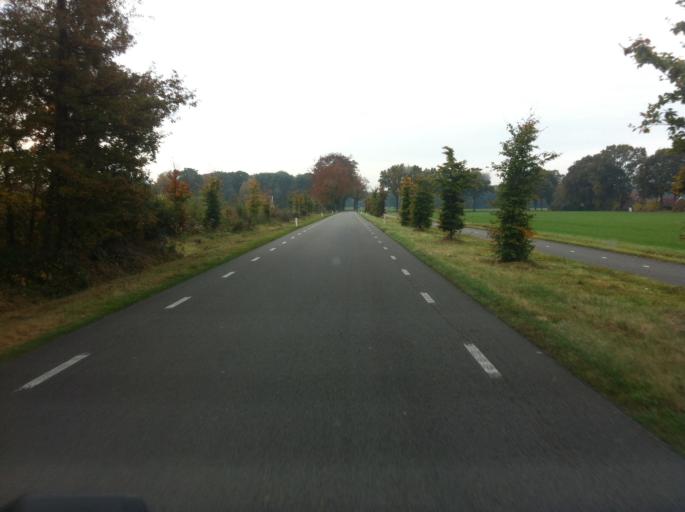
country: NL
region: Gelderland
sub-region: Gemeente Winterswijk
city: Winterswijk
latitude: 51.9854
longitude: 6.7609
